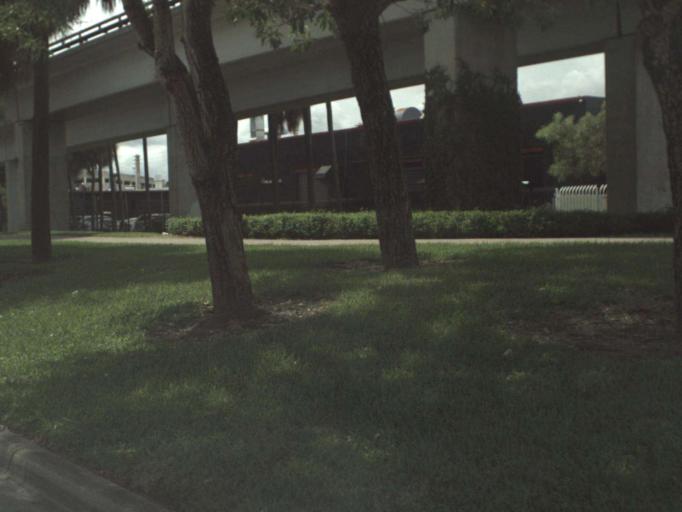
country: US
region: Florida
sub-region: Miami-Dade County
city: South Miami
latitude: 25.7068
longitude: -80.2867
